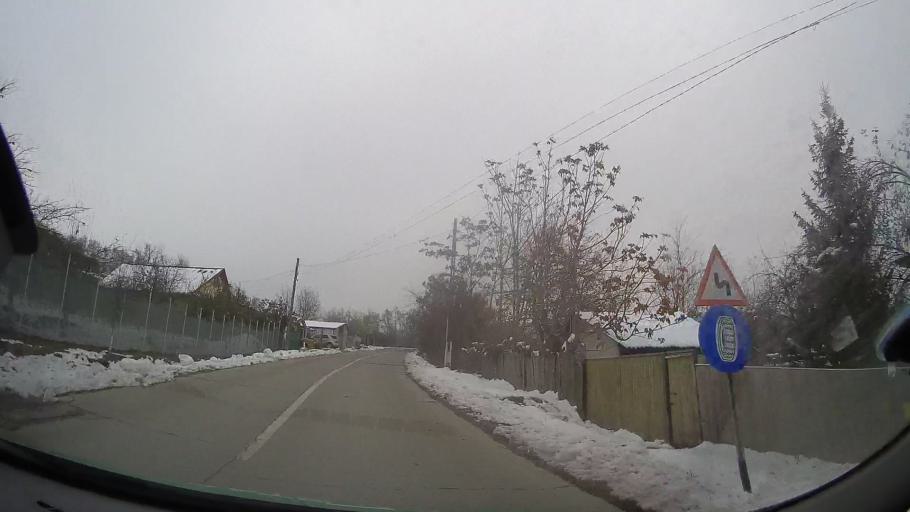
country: RO
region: Bacau
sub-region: Comuna Podu Turcului
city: Podu Turcului
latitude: 46.2023
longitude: 27.3910
